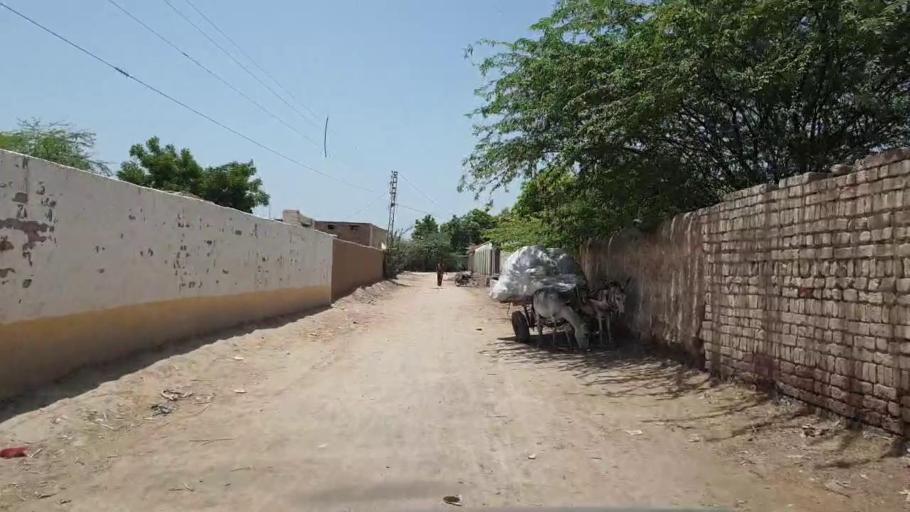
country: PK
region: Sindh
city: Sakrand
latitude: 26.1073
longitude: 68.3913
